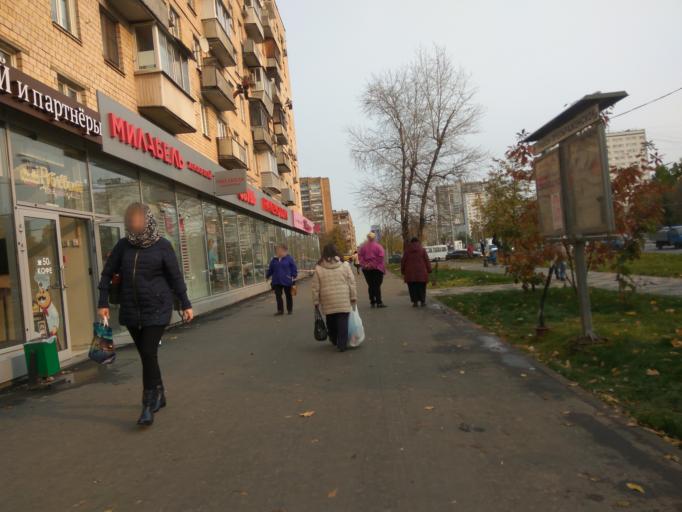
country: RU
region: Moskovskaya
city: Bogorodskoye
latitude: 55.7974
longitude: 37.7209
